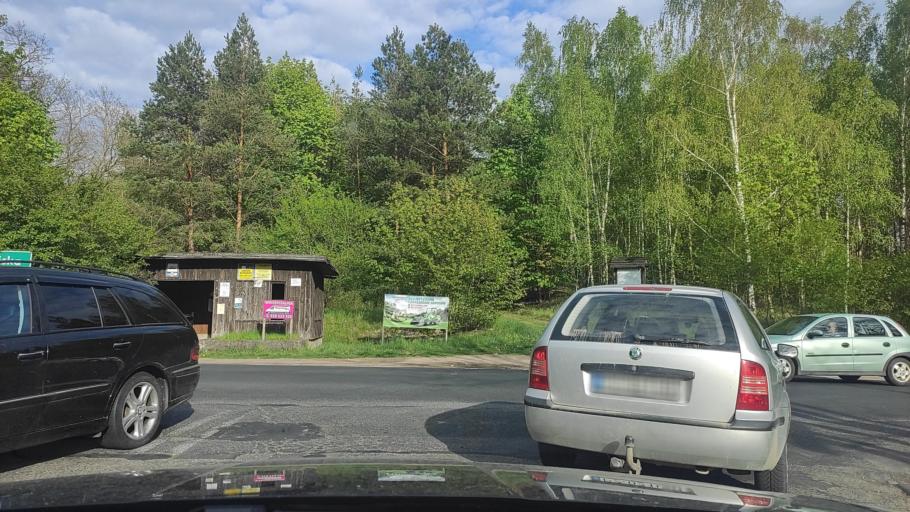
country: PL
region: Greater Poland Voivodeship
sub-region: Powiat poznanski
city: Pobiedziska
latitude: 52.4511
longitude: 17.2478
